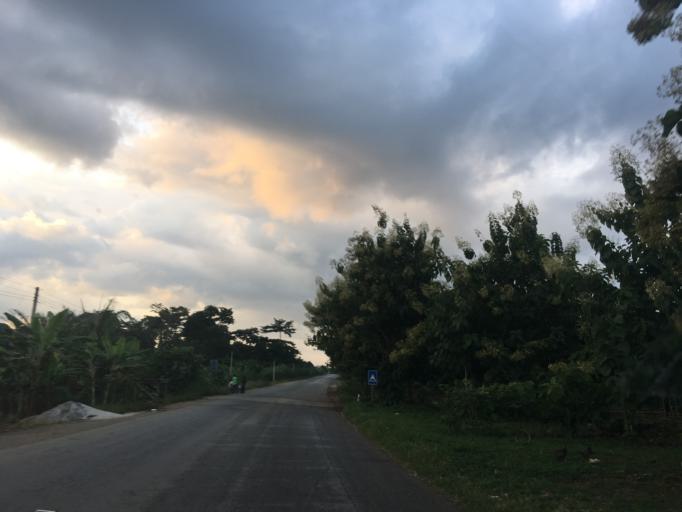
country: GH
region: Western
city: Bibiani
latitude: 6.7506
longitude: -2.5045
